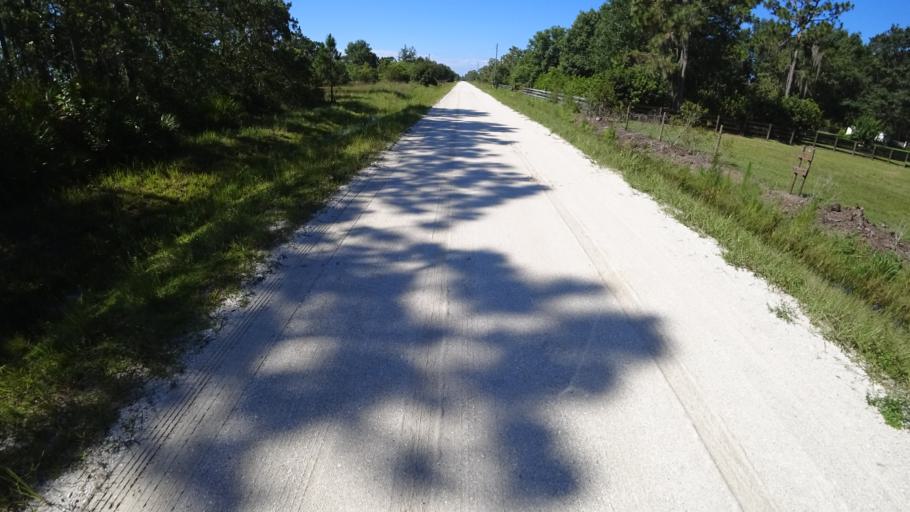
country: US
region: Florida
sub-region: Sarasota County
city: The Meadows
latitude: 27.4116
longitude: -82.2915
